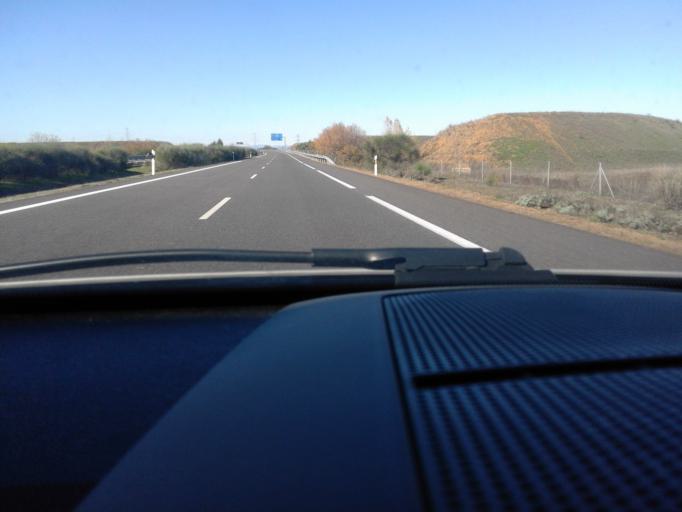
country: ES
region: Castille and Leon
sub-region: Provincia de Leon
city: Santas Martas
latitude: 42.4415
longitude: -5.3546
